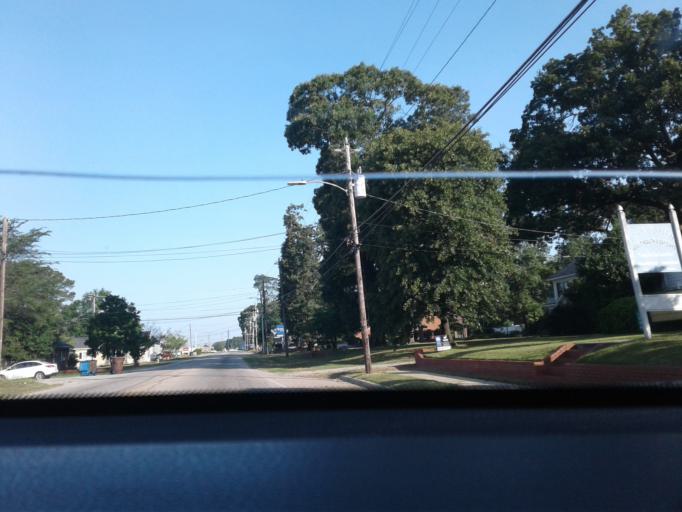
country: US
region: North Carolina
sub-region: Harnett County
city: Dunn
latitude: 35.3139
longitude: -78.6203
